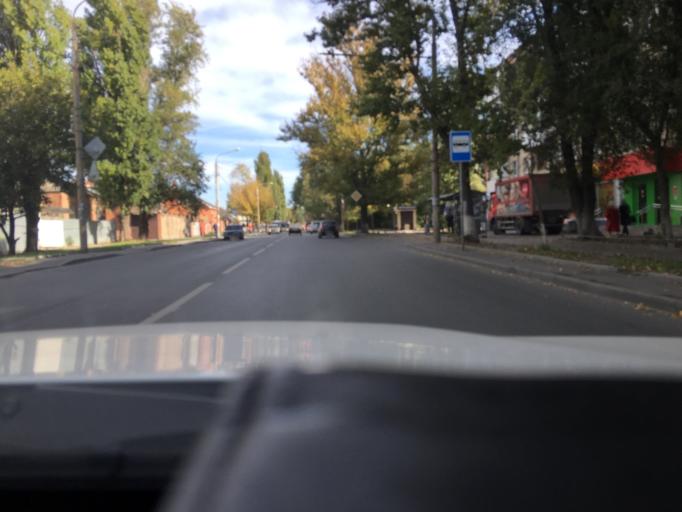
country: RU
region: Rostov
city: Imeni Chkalova
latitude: 47.2695
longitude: 39.7892
